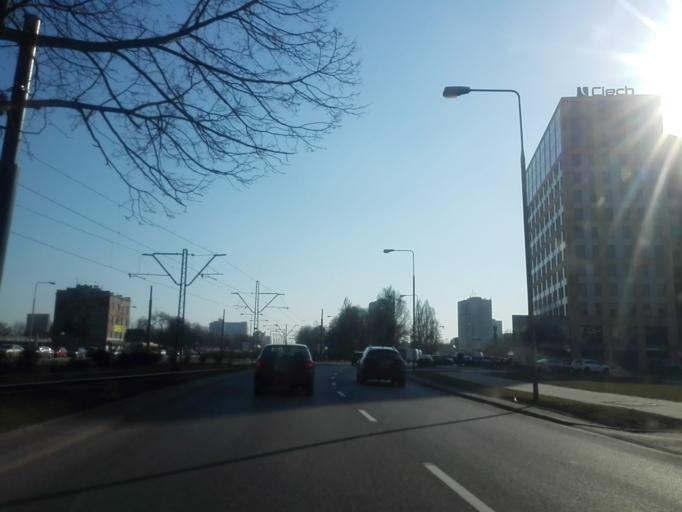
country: PL
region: Masovian Voivodeship
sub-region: Warszawa
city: Mokotow
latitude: 52.1827
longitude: 21.0231
